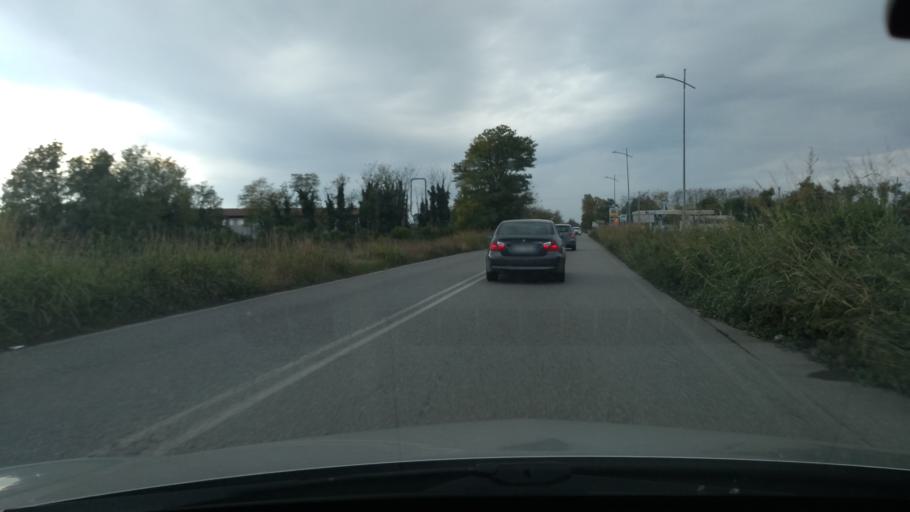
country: IT
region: Lombardy
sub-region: Provincia di Bergamo
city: Urgnano
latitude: 45.5924
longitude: 9.6817
